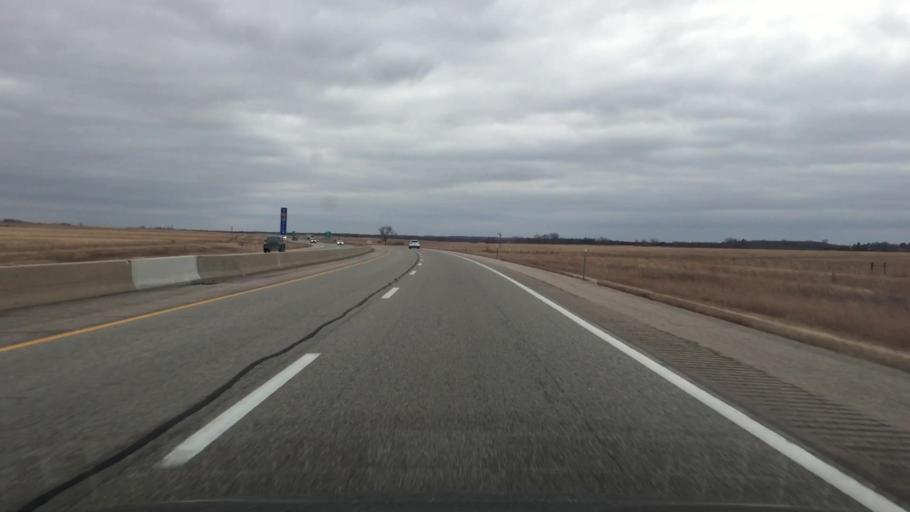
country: US
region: Kansas
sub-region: Butler County
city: El Dorado
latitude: 37.8988
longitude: -96.8330
